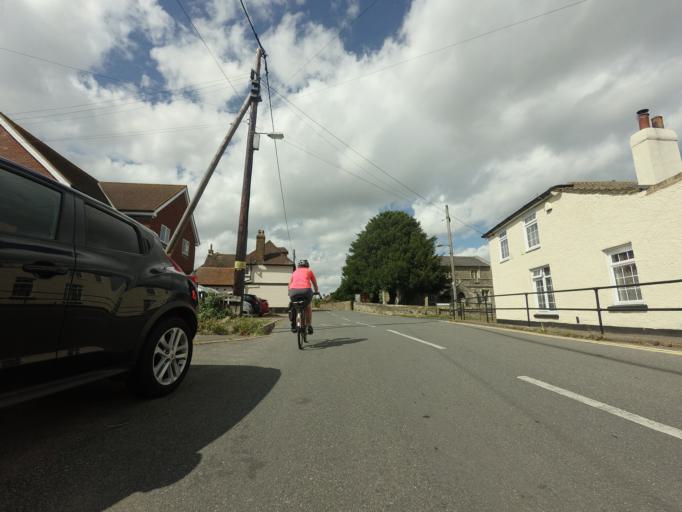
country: GB
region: England
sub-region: Medway
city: Allhallows
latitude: 51.4667
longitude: 0.6414
